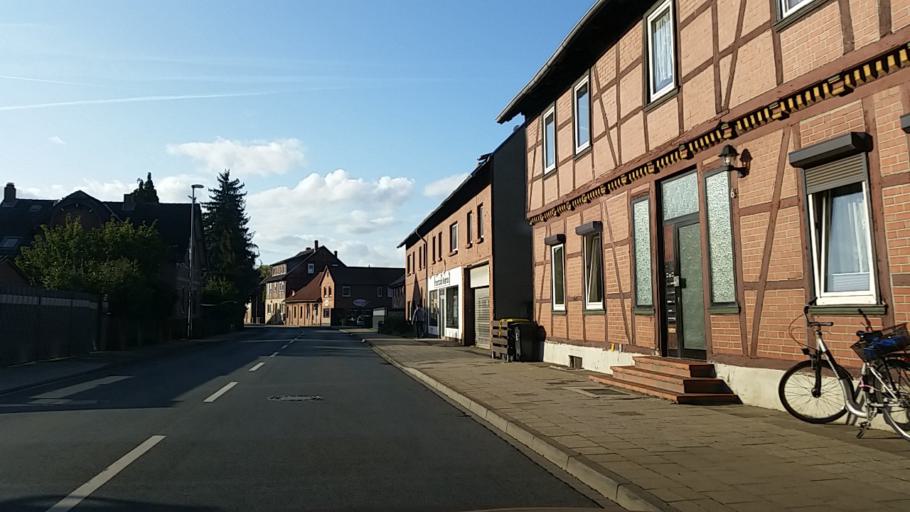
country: DE
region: Lower Saxony
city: Vordorf
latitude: 52.3173
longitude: 10.5290
